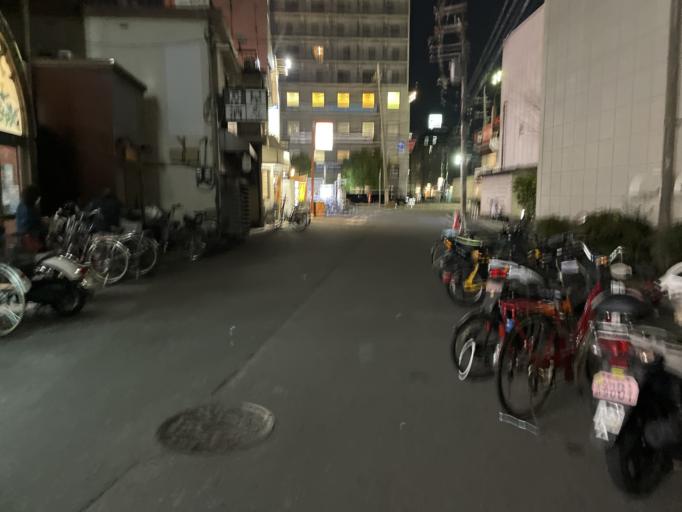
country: JP
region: Osaka
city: Yao
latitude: 34.6649
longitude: 135.5883
